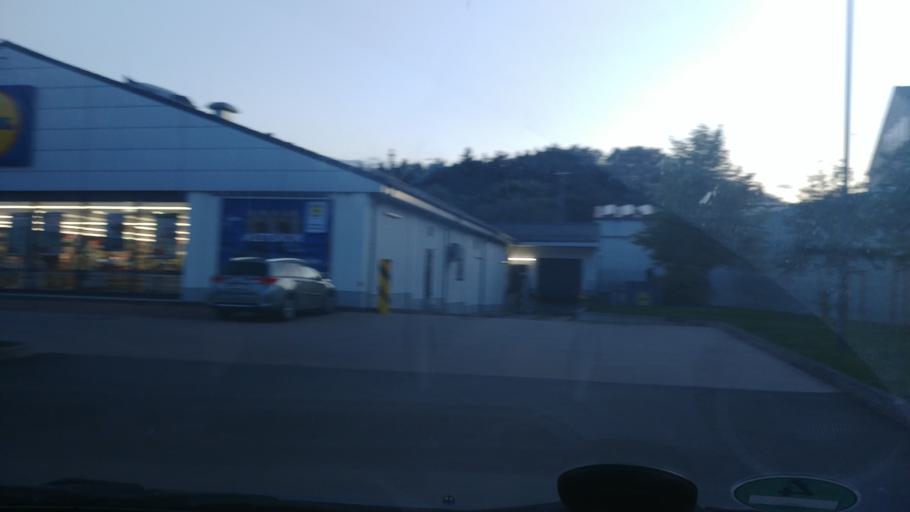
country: DE
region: Lower Saxony
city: Uslar
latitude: 51.6609
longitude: 9.6290
